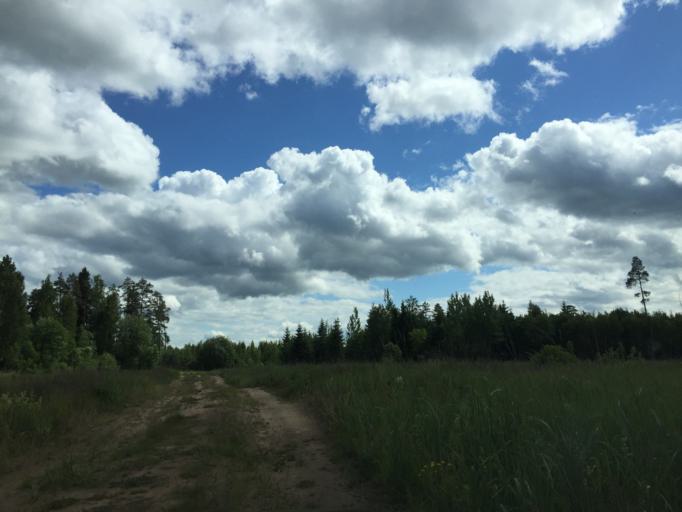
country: LV
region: Lecava
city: Iecava
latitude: 56.5504
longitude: 24.3422
